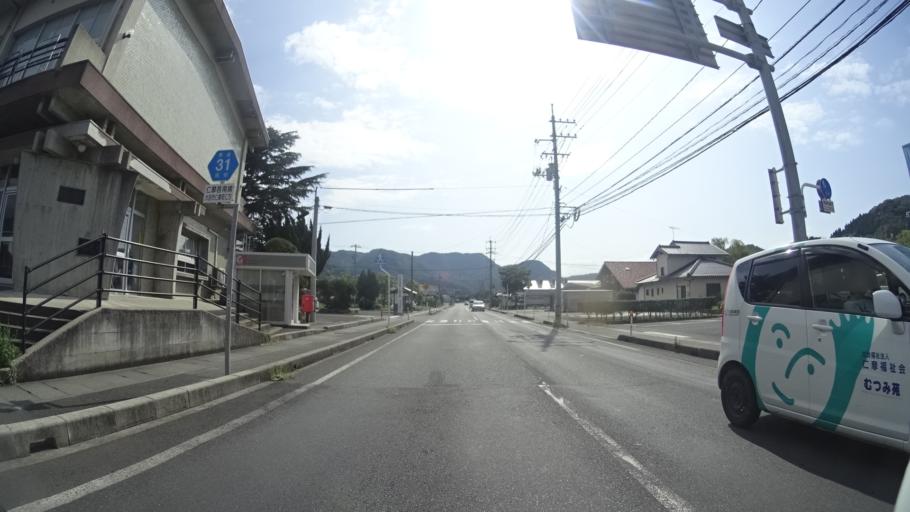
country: JP
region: Shimane
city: Odacho-oda
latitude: 35.1480
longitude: 132.4058
